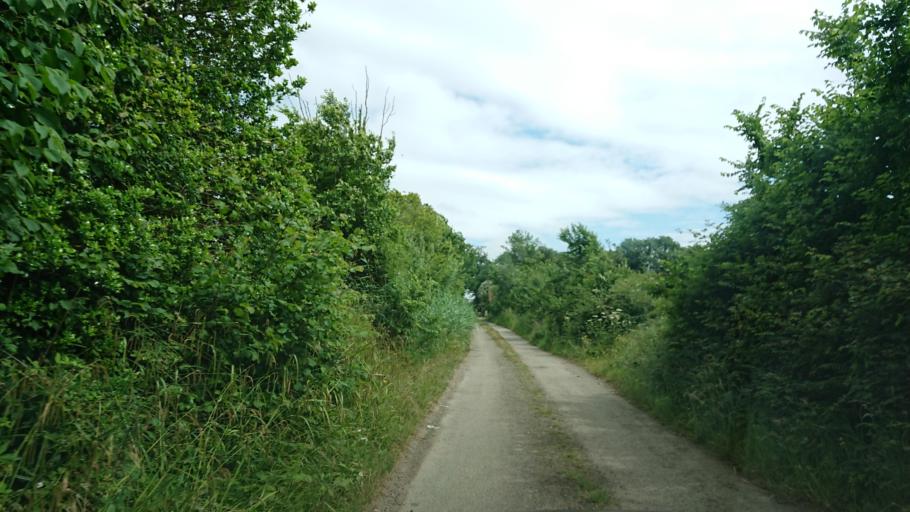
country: IE
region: Munster
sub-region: Waterford
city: Waterford
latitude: 52.2767
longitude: -7.1517
